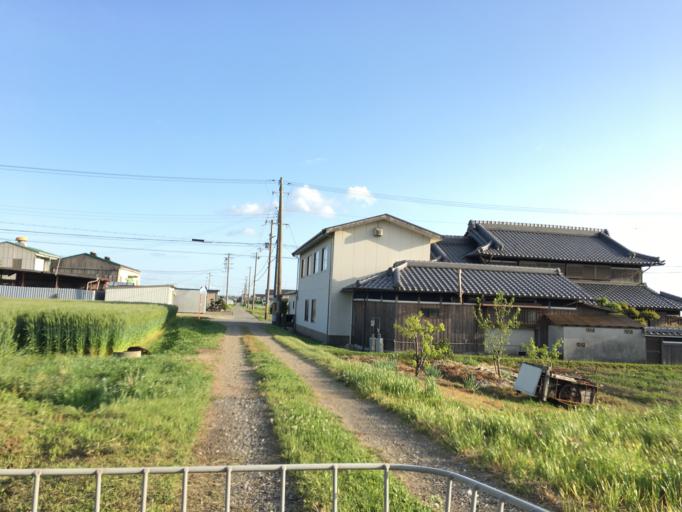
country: JP
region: Hyogo
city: Miki
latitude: 34.7382
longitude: 134.9493
